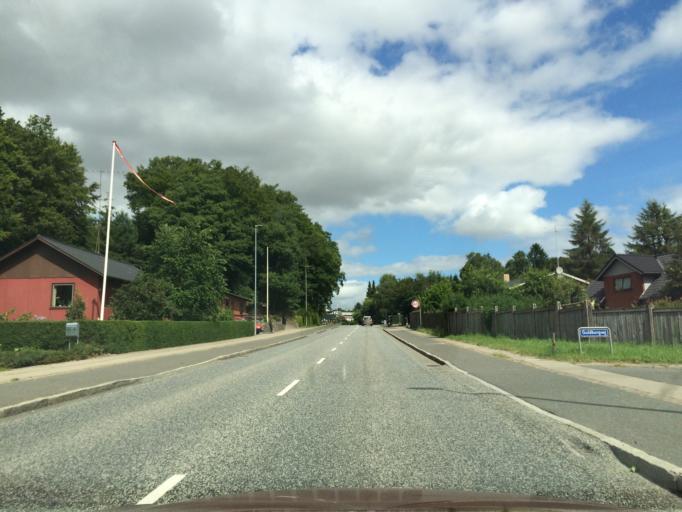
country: DK
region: Central Jutland
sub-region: Silkeborg Kommune
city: Silkeborg
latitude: 56.1925
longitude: 9.5827
